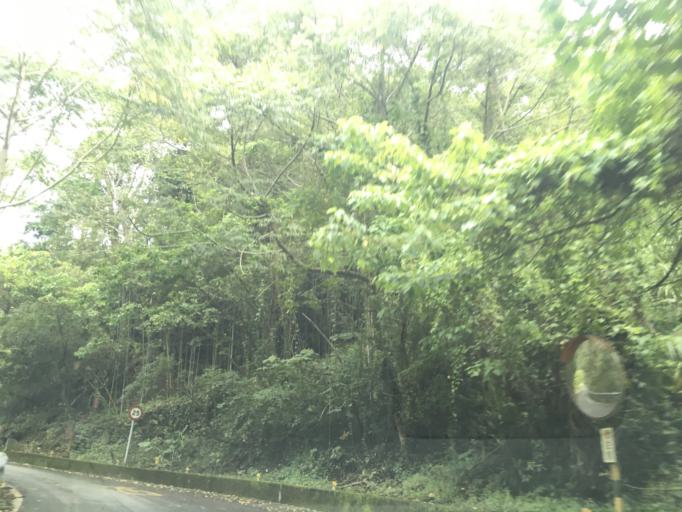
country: TW
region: Taiwan
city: Lugu
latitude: 23.5345
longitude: 120.7058
